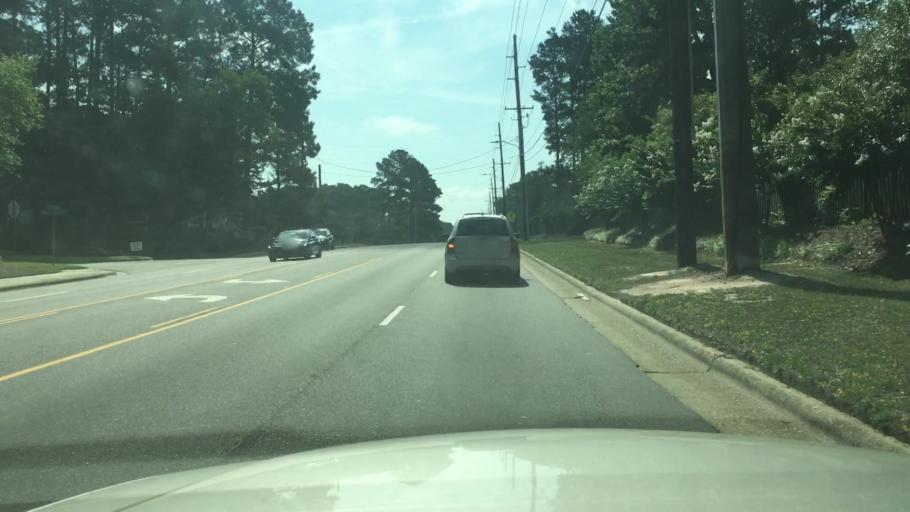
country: US
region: North Carolina
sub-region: Cumberland County
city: Fayetteville
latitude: 35.0662
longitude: -78.9462
